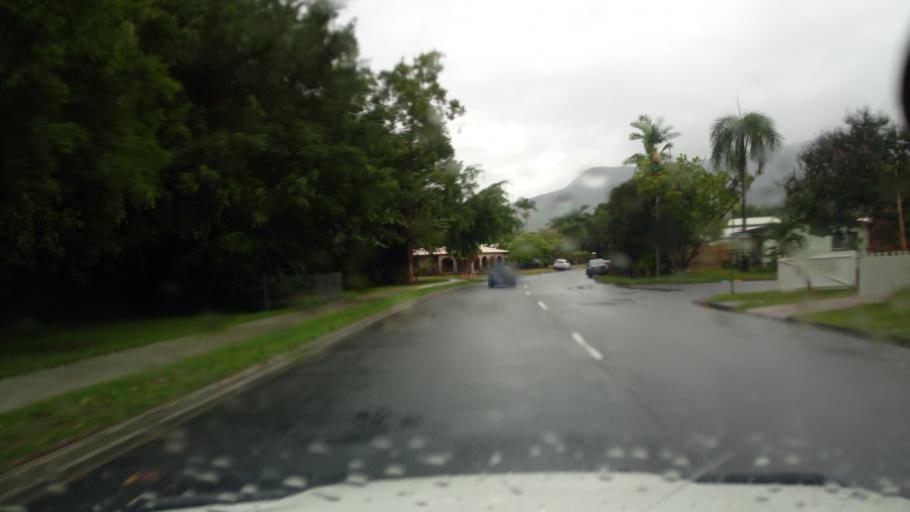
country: AU
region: Queensland
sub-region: Cairns
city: Woree
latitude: -16.9354
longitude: 145.7337
